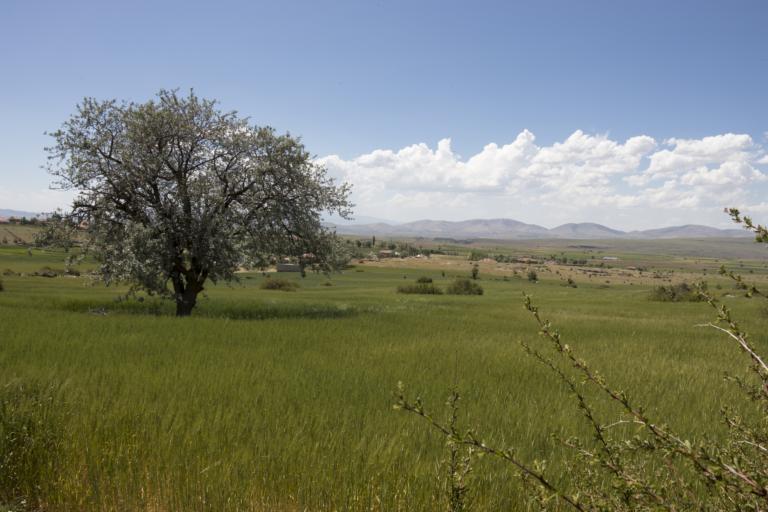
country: TR
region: Kayseri
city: Toklar
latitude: 38.4204
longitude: 36.1052
